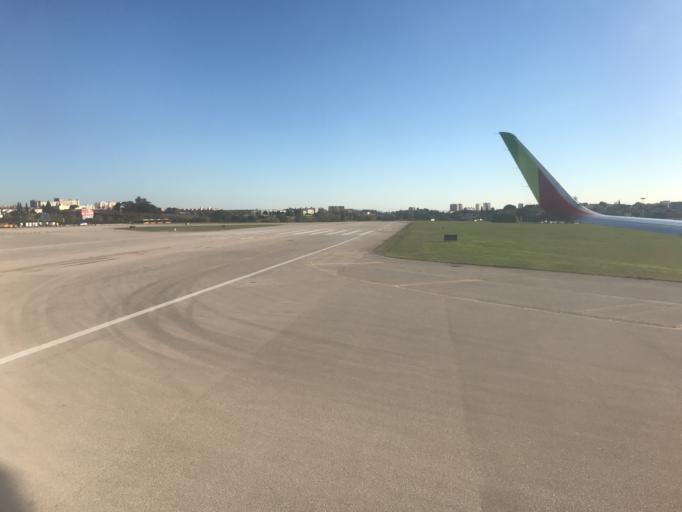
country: PT
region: Lisbon
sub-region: Loures
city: Moscavide
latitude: 38.7677
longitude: -9.1325
